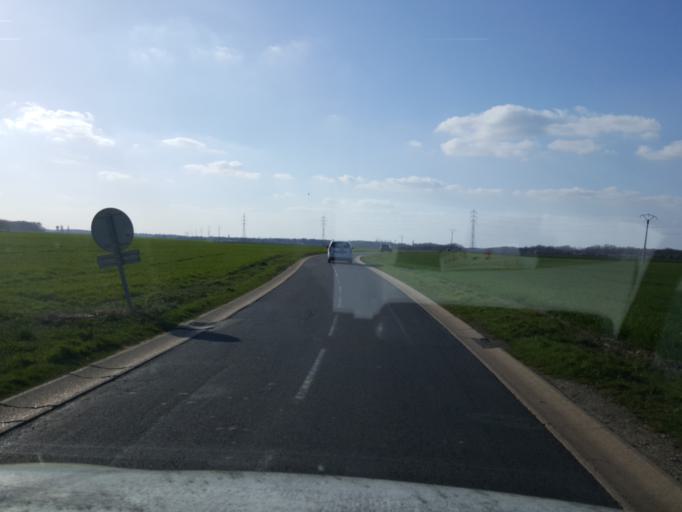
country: FR
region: Ile-de-France
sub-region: Departement des Yvelines
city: Gazeran
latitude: 48.6241
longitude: 1.8037
